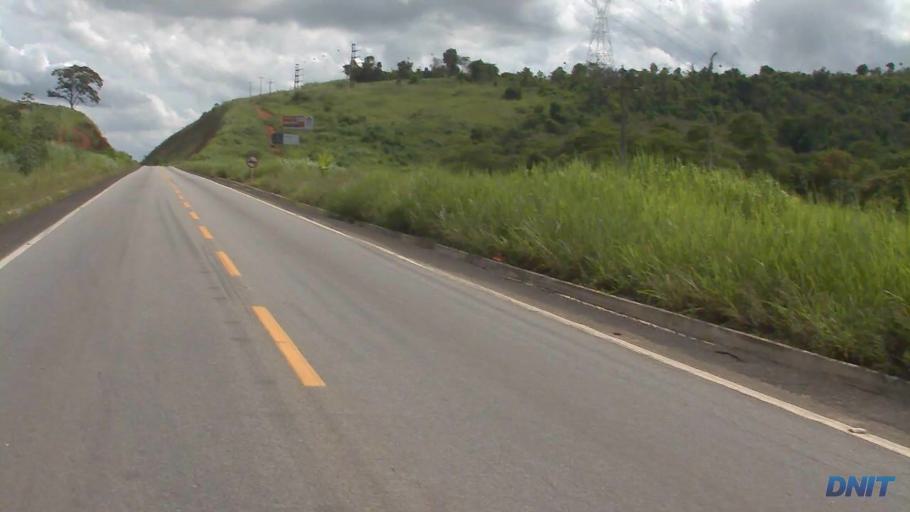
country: BR
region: Minas Gerais
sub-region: Ipatinga
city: Ipatinga
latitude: -19.4151
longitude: -42.4918
